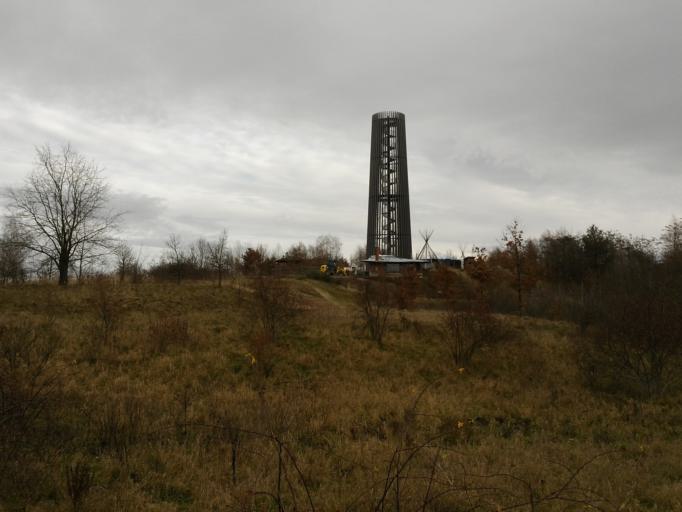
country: DE
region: Saxony
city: Zwenkau
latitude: 51.2545
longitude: 12.3223
